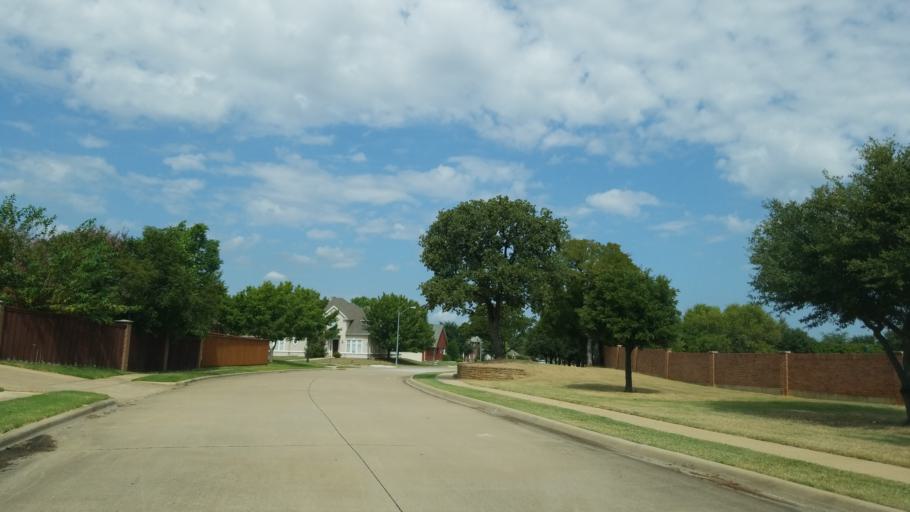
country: US
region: Texas
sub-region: Tarrant County
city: Grapevine
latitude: 32.8971
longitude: -97.1013
